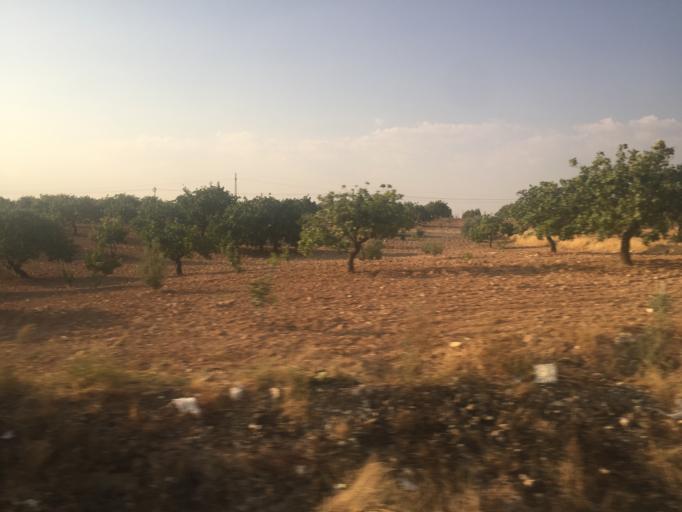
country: TR
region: Sanliurfa
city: Birecik
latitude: 37.0168
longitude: 37.8891
